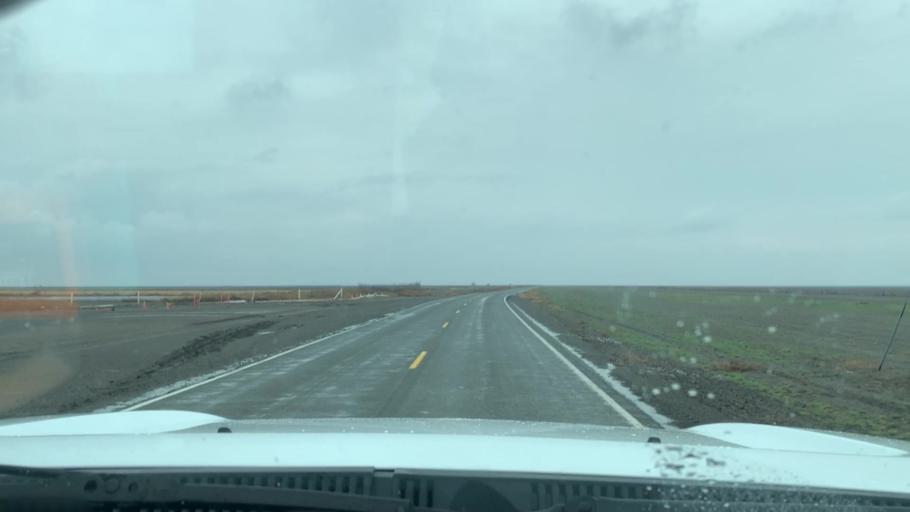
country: US
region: California
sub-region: Tulare County
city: Alpaugh
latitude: 35.9339
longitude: -119.6472
